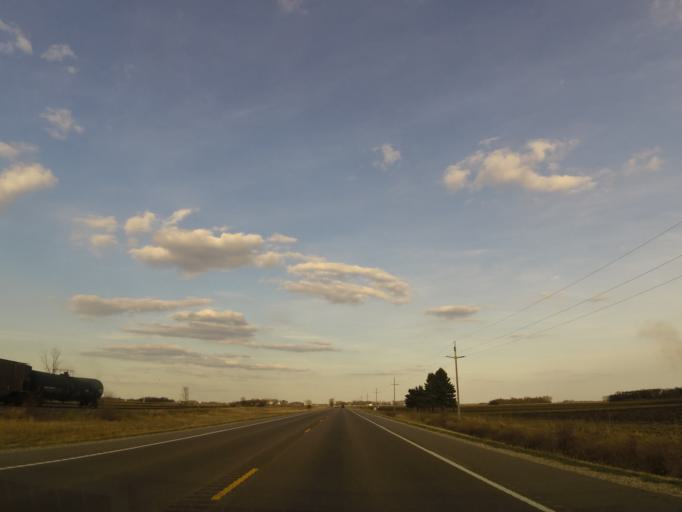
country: US
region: Minnesota
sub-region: McLeod County
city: Hutchinson
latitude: 44.7225
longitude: -94.4544
